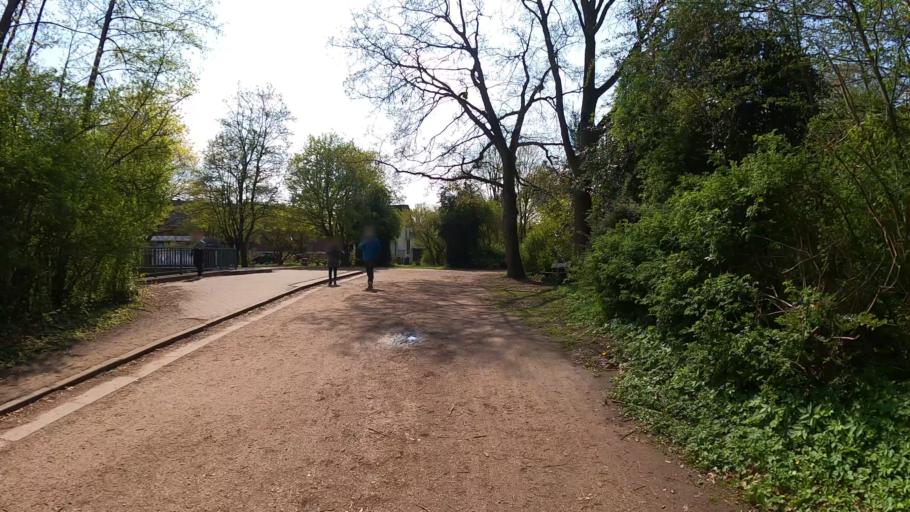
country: DE
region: Hamburg
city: Steilshoop
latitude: 53.6172
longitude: 10.0701
